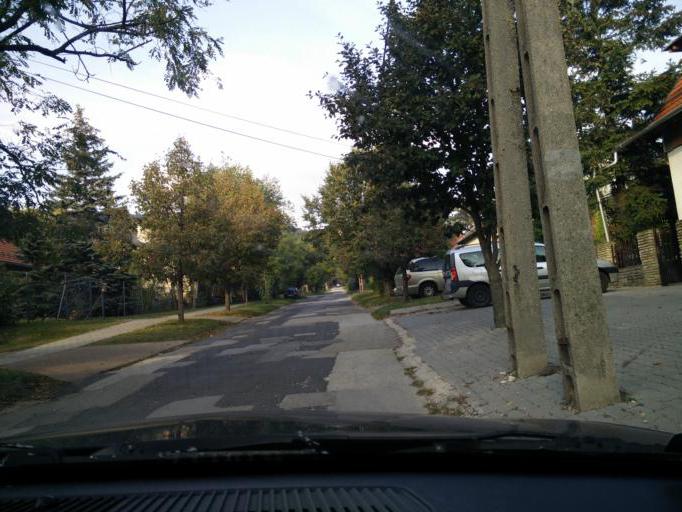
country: HU
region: Pest
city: Piliscsaba
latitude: 47.6388
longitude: 18.8353
